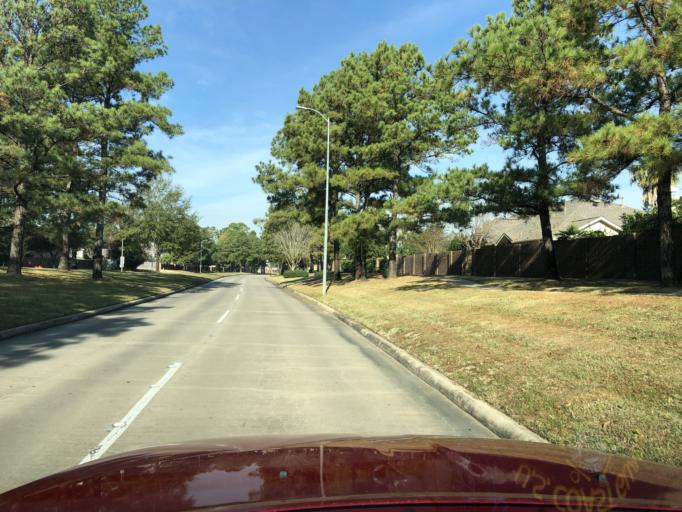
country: US
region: Texas
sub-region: Harris County
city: Tomball
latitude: 30.0297
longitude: -95.5644
